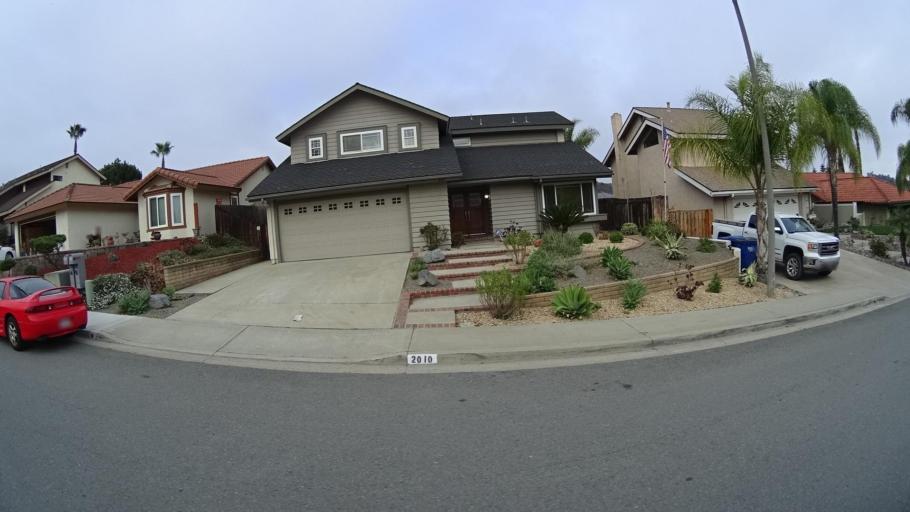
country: US
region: California
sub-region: San Diego County
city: Rancho San Diego
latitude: 32.7546
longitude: -116.9172
